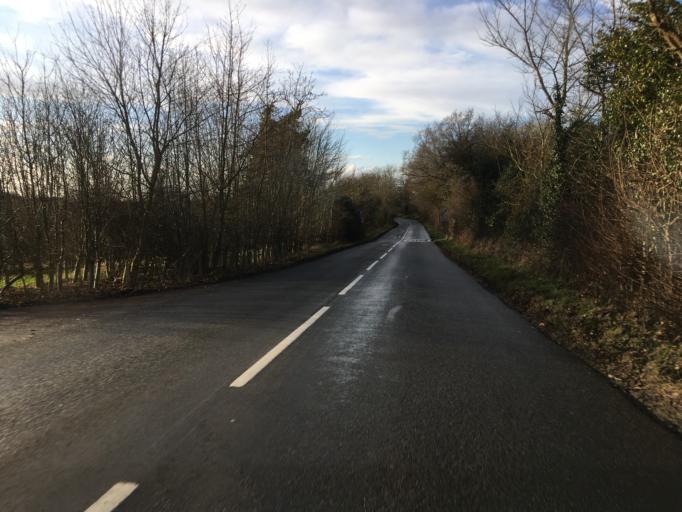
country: GB
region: England
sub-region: Warwickshire
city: Henley in Arden
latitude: 52.2260
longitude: -1.7786
